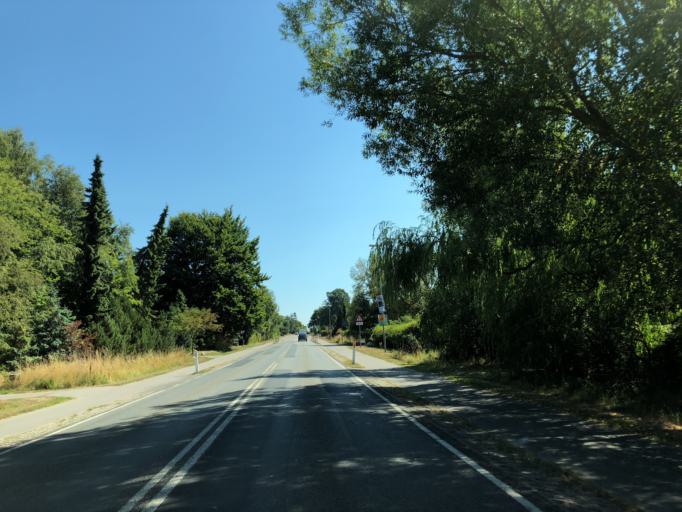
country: DK
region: Zealand
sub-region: Odsherred Kommune
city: Nykobing Sjaelland
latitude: 55.9421
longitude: 11.7369
